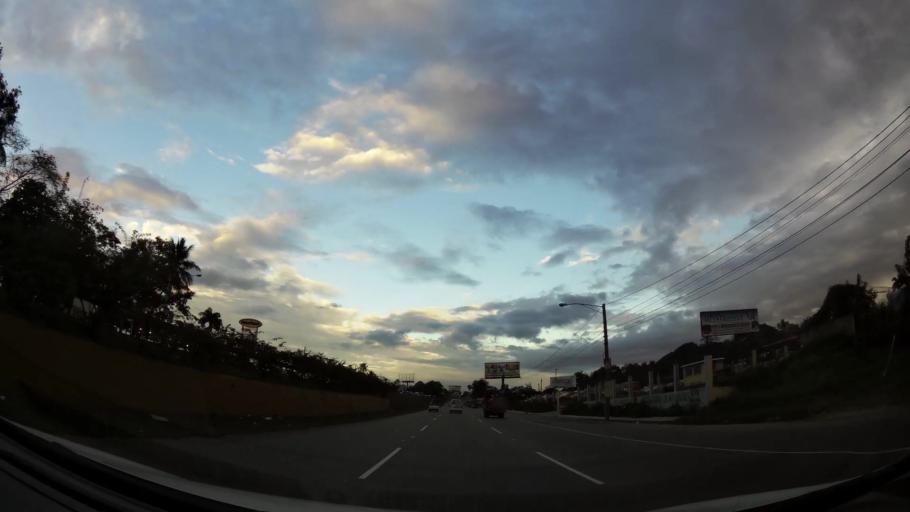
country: DO
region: Santo Domingo
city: Santo Domingo Oeste
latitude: 18.5373
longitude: -70.0213
